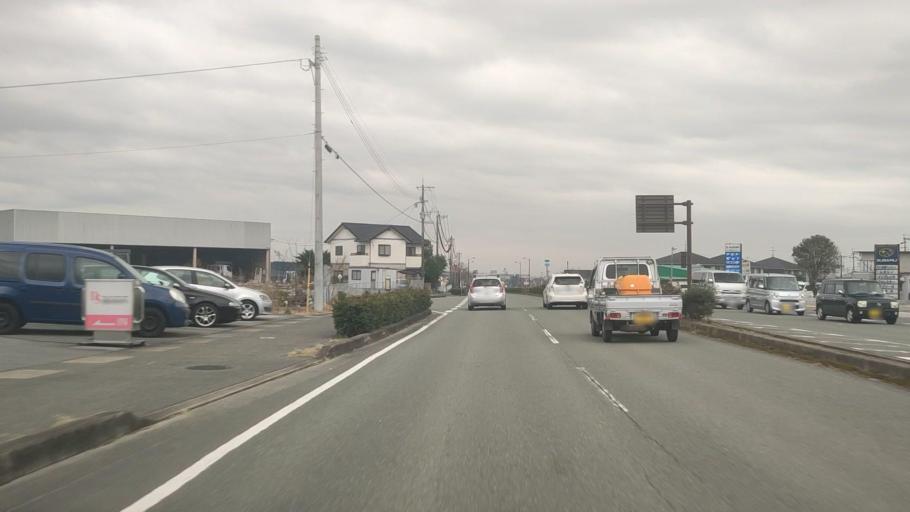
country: JP
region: Kumamoto
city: Ozu
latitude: 32.8329
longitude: 130.7999
